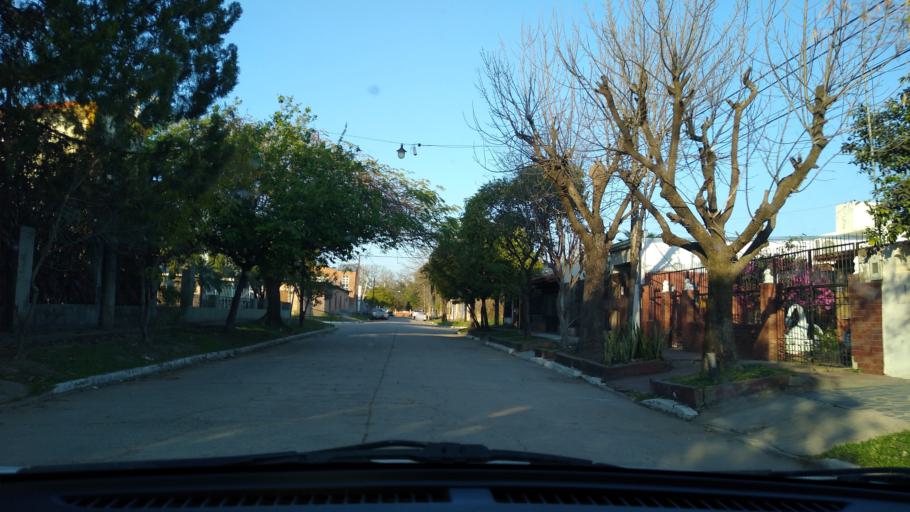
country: AR
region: Chaco
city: Barranqueras
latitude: -27.4775
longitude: -58.9535
